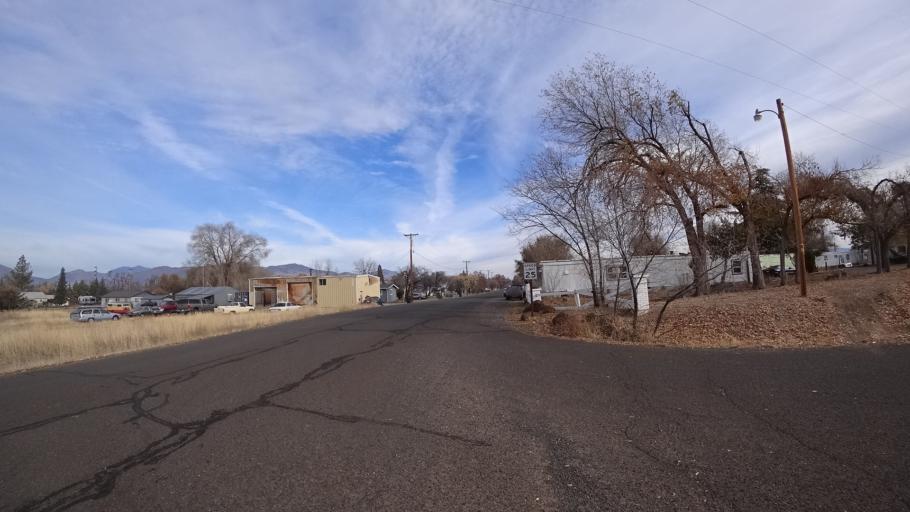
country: US
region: California
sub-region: Siskiyou County
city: Montague
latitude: 41.7246
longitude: -122.5334
